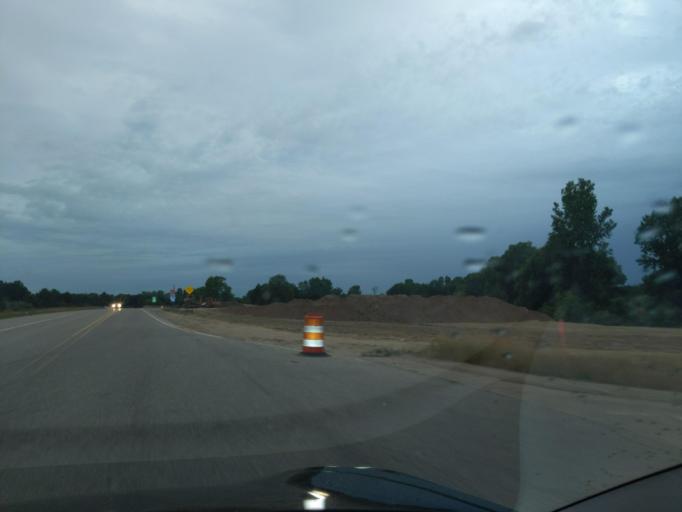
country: US
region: Michigan
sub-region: Clinton County
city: DeWitt
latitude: 42.8102
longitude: -84.6027
